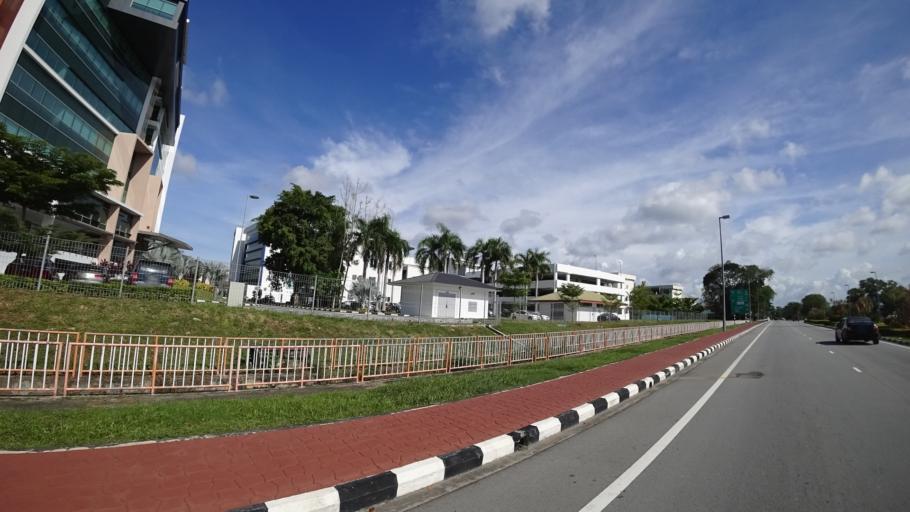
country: BN
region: Brunei and Muara
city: Bandar Seri Begawan
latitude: 4.9376
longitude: 114.9411
